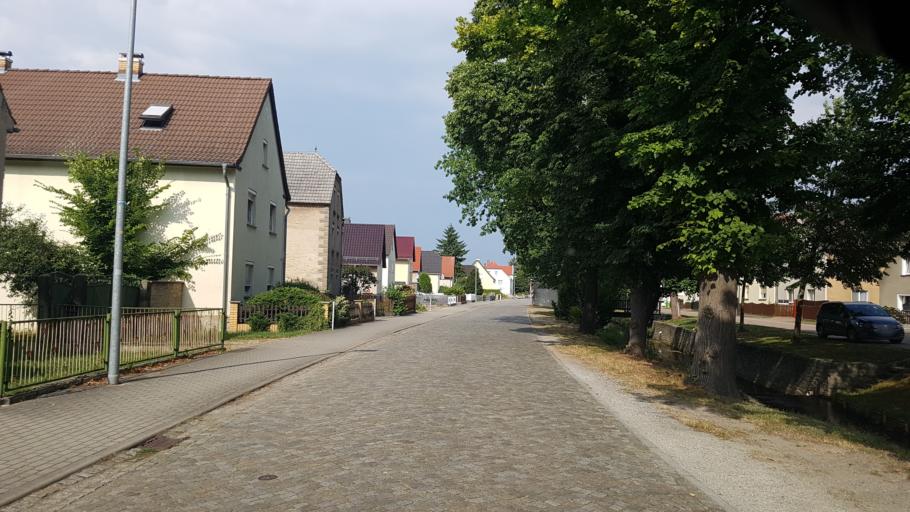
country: DE
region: Brandenburg
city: Grossthiemig
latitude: 51.3841
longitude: 13.6776
